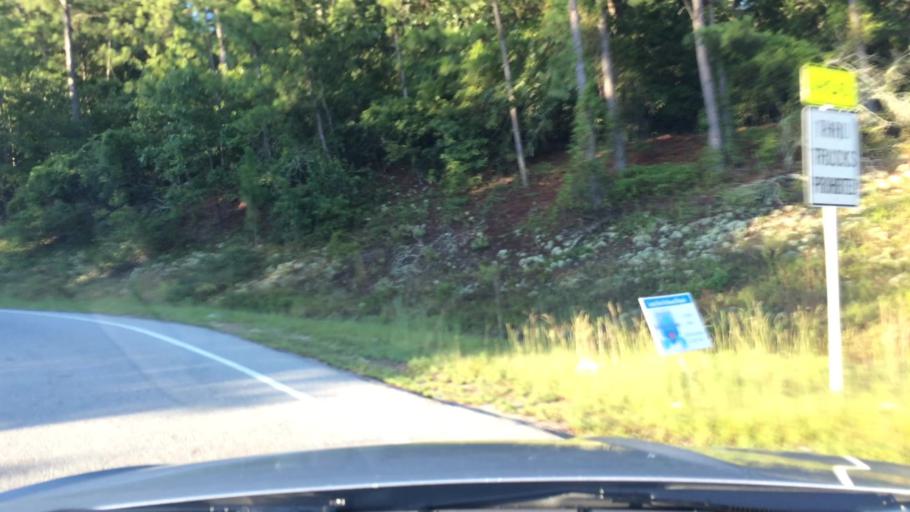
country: US
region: South Carolina
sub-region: Calhoun County
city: Oak Grove
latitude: 33.8110
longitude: -81.0104
